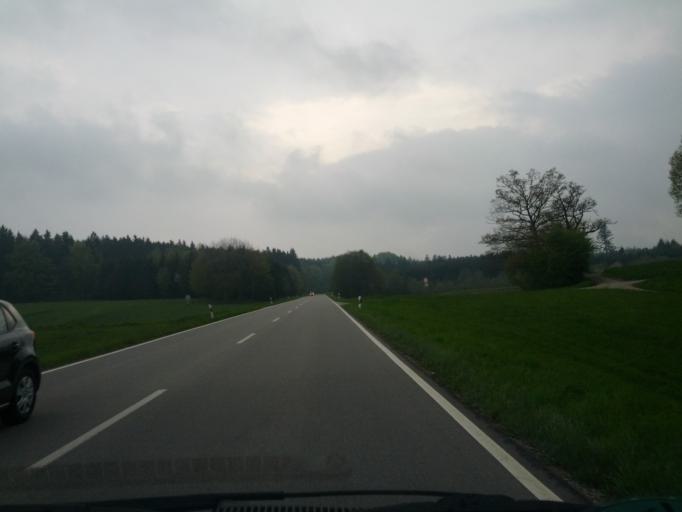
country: DE
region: Baden-Wuerttemberg
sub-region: Freiburg Region
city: Hasel
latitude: 47.6476
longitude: 7.8772
